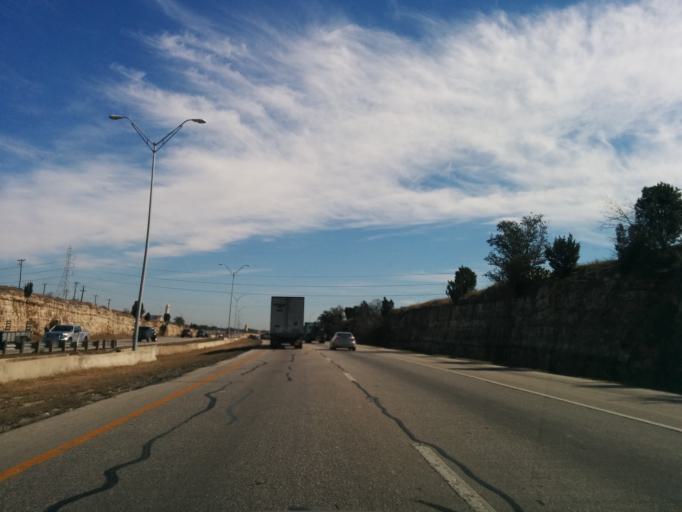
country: US
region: Texas
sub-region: Bexar County
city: Shavano Park
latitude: 29.6033
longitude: -98.5333
